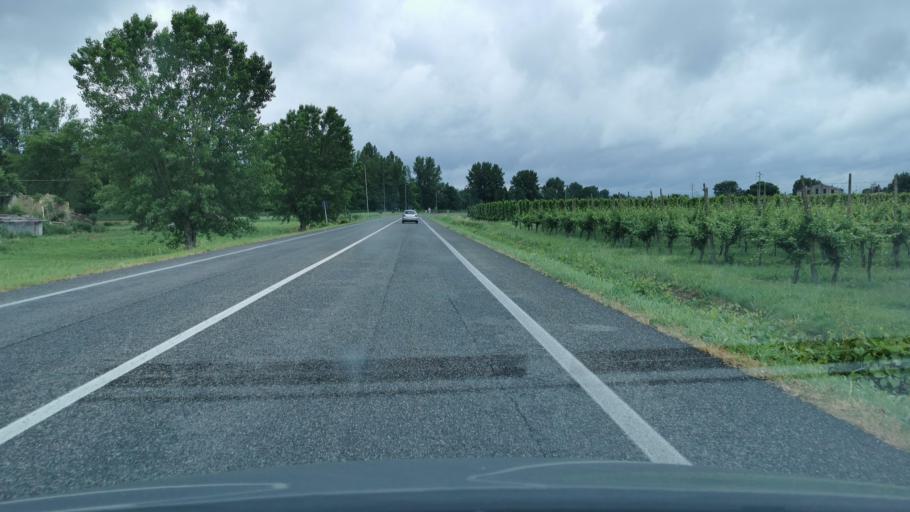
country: IT
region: Emilia-Romagna
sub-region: Provincia di Ravenna
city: Granarolo
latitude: 44.3523
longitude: 11.9274
